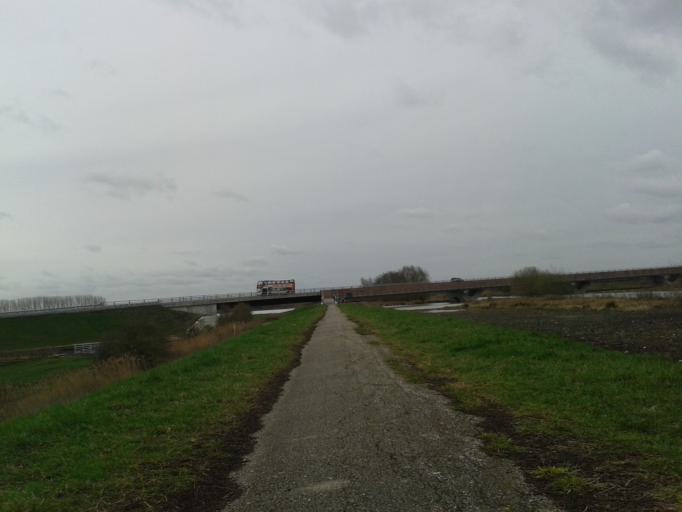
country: GB
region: England
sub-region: Cambridgeshire
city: Ely
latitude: 52.3855
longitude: 0.2675
